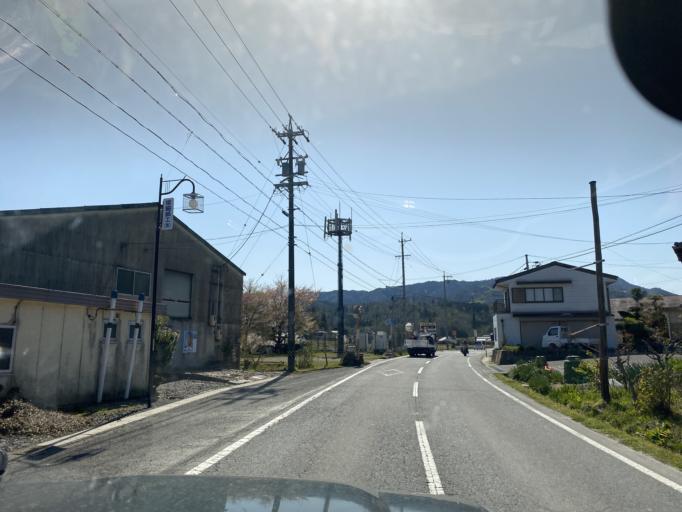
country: JP
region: Mie
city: Ueno-ebisumachi
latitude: 34.8433
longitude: 136.1295
